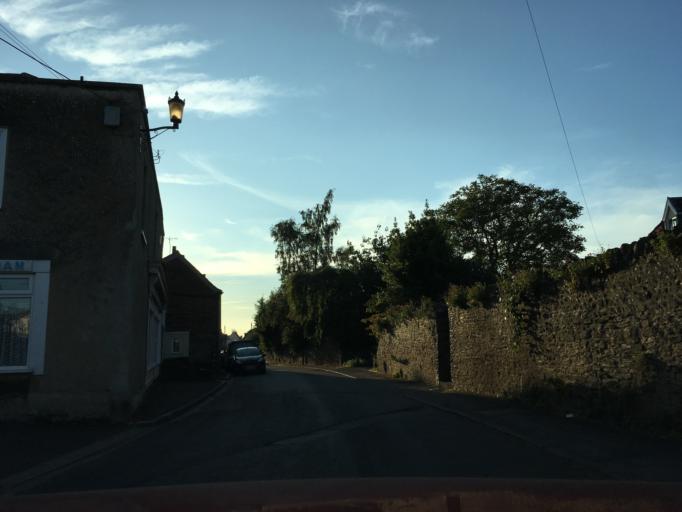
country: GB
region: England
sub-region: South Gloucestershire
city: Tytherington
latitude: 51.5497
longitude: -2.4635
